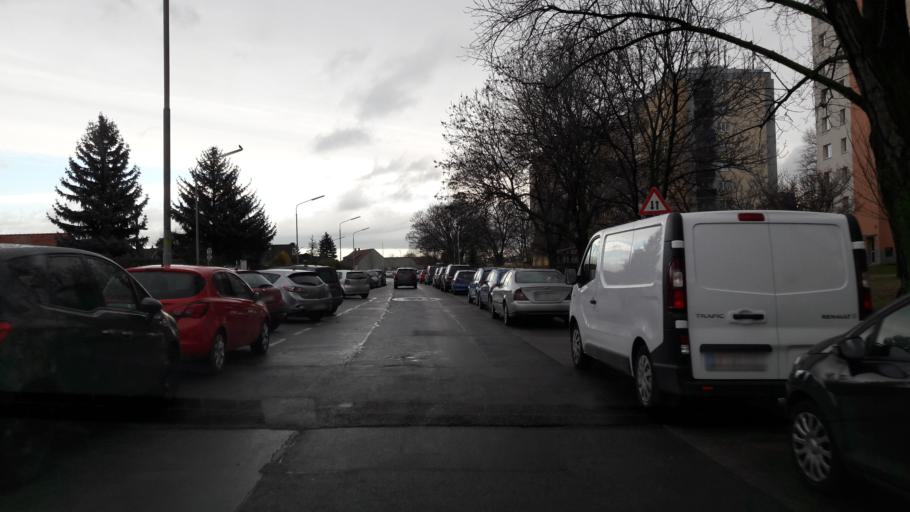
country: AT
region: Lower Austria
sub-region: Politischer Bezirk Wien-Umgebung
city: Schwechat
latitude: 48.1700
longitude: 16.4328
